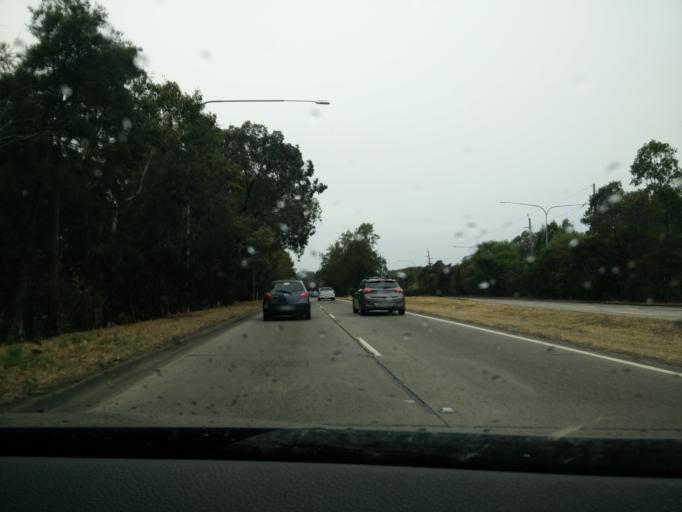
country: AU
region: New South Wales
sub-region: Parramatta
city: Constitution Hill
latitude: -33.7747
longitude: 150.9618
